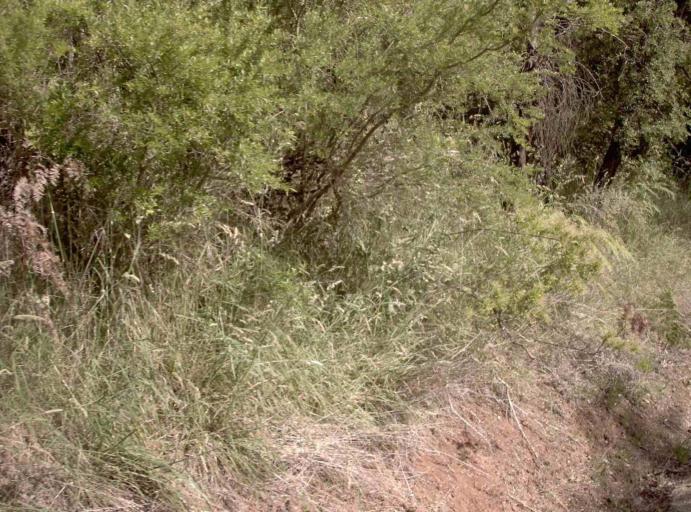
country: AU
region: Victoria
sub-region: East Gippsland
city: Lakes Entrance
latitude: -37.5182
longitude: 148.1620
